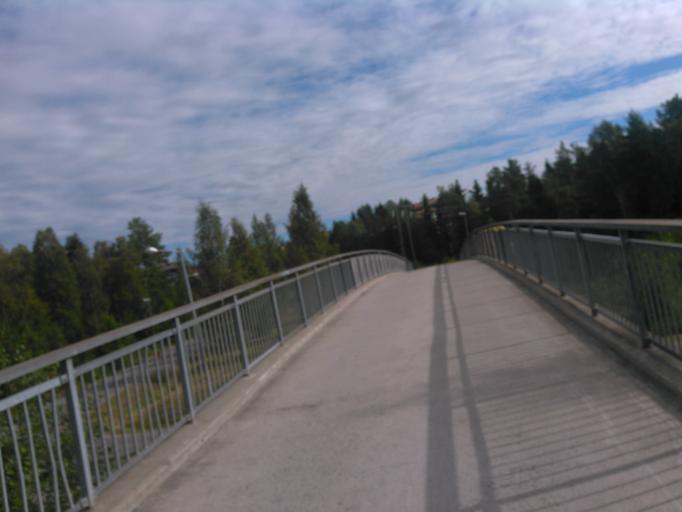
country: SE
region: Vaesterbotten
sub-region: Umea Kommun
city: Ersmark
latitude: 63.8232
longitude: 20.3234
